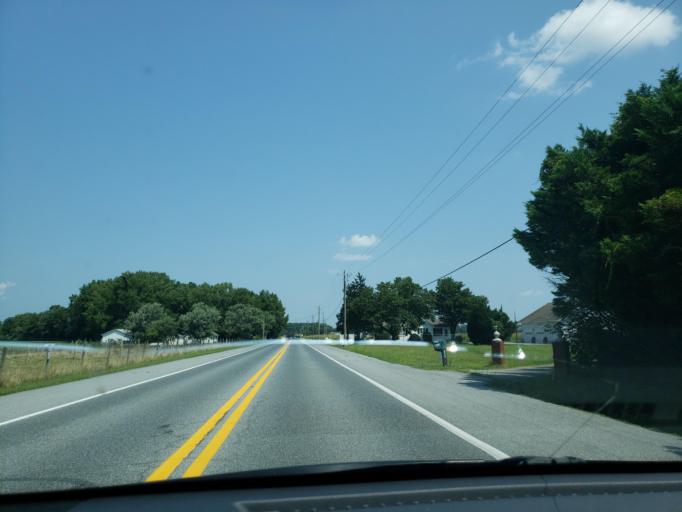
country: US
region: Delaware
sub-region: Sussex County
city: Milton
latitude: 38.8086
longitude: -75.3143
